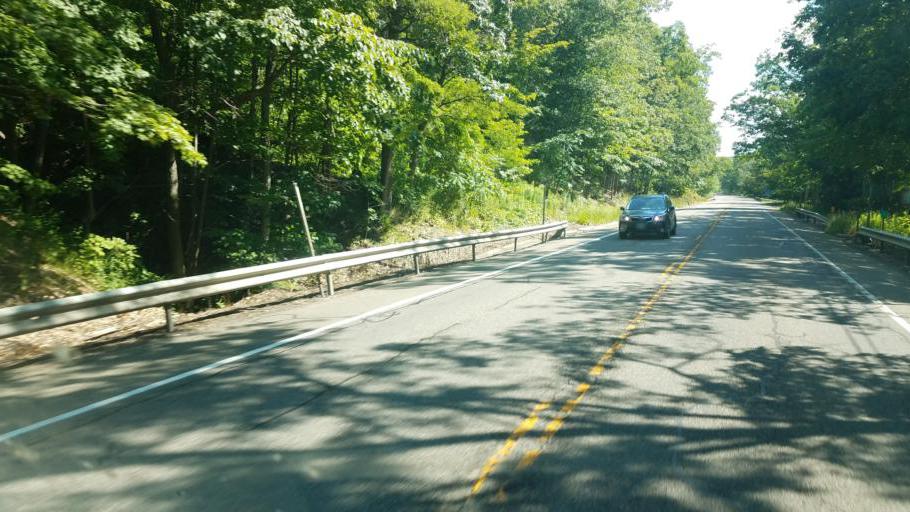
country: US
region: New York
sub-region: Steuben County
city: Sylvan Beach
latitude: 42.4571
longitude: -77.1639
